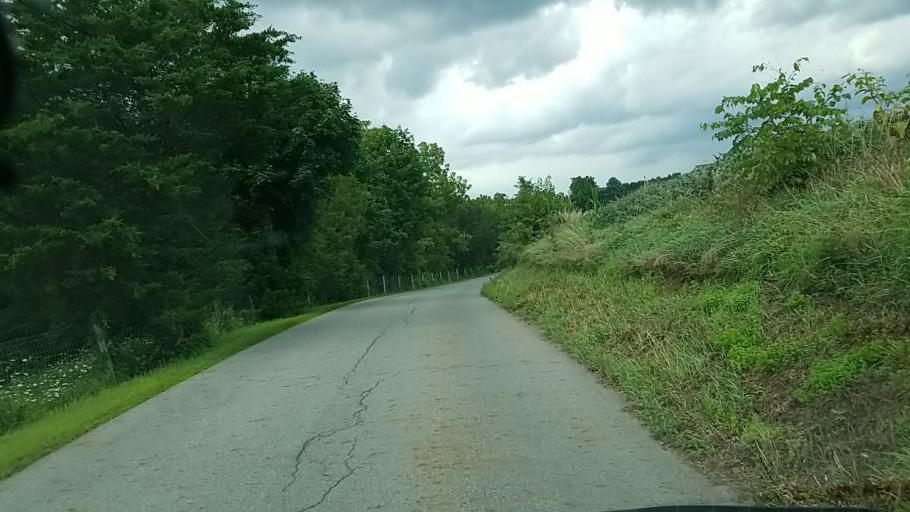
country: US
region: Pennsylvania
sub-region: Dauphin County
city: Elizabethville
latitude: 40.5919
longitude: -76.8023
